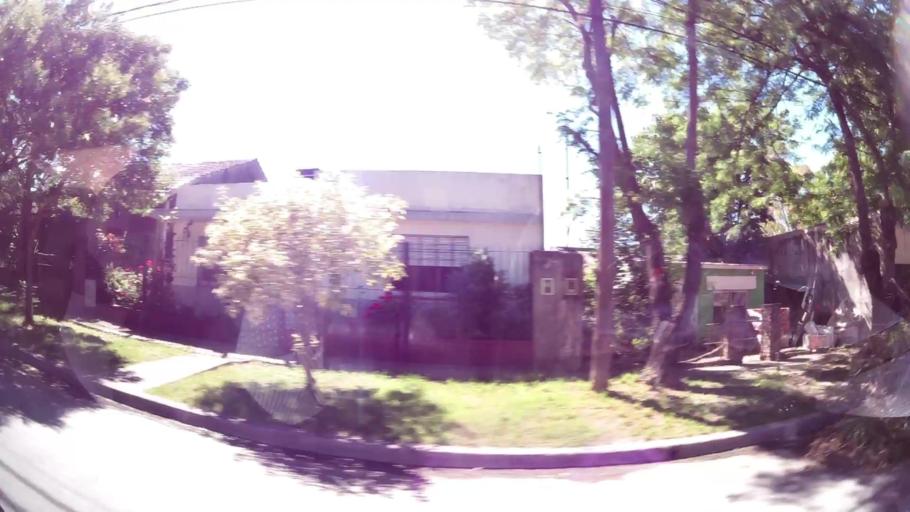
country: AR
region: Buenos Aires
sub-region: Partido de Tigre
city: Tigre
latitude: -34.5039
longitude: -58.6157
